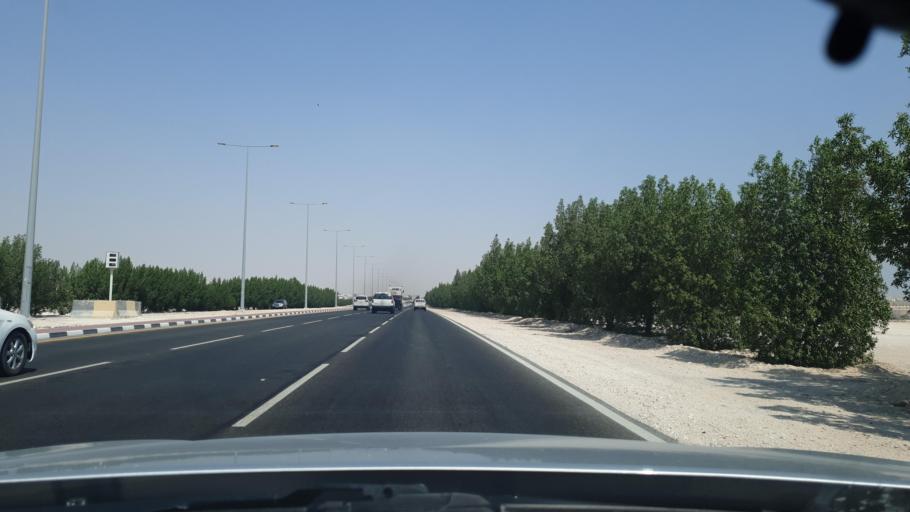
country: QA
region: Al Khawr
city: Al Khawr
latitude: 25.7028
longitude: 51.5038
